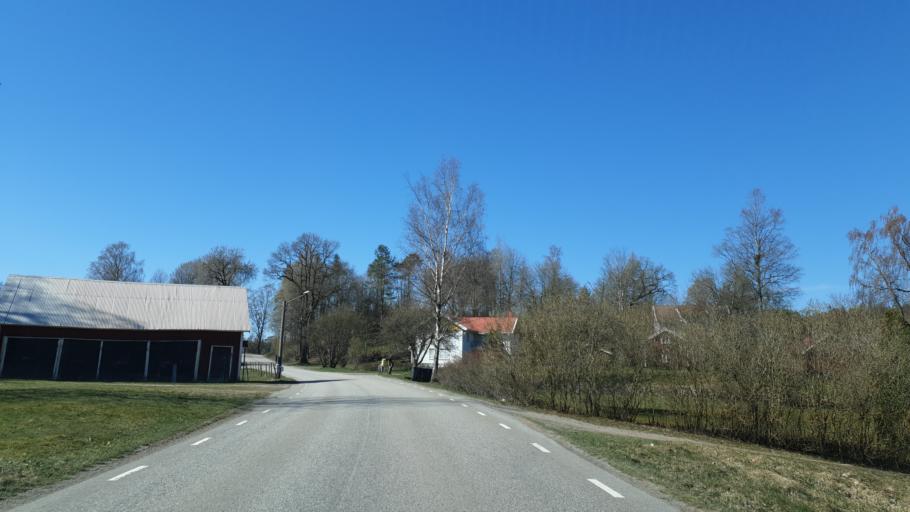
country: SE
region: Vaestra Goetaland
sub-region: Svenljunga Kommun
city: Svenljunga
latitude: 57.4401
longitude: 13.1267
